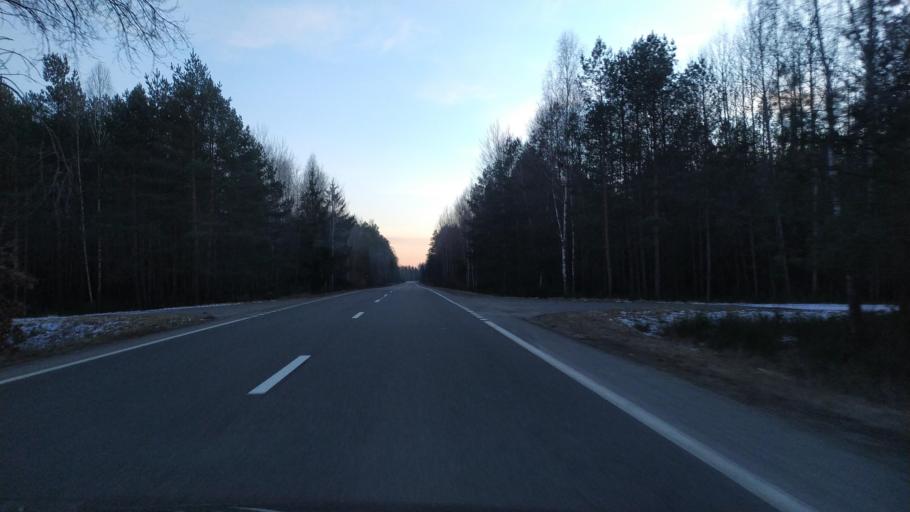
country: BY
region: Brest
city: Pruzhany
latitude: 52.5099
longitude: 24.1782
